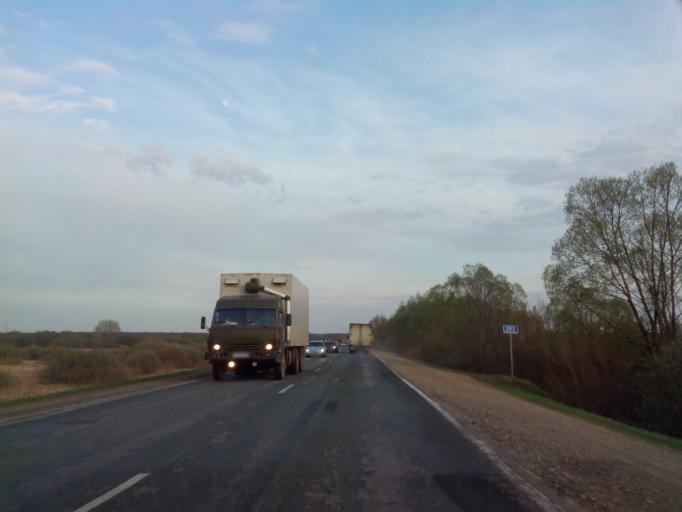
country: RU
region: Rjazan
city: Ryazhsk
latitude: 53.7194
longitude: 39.9154
